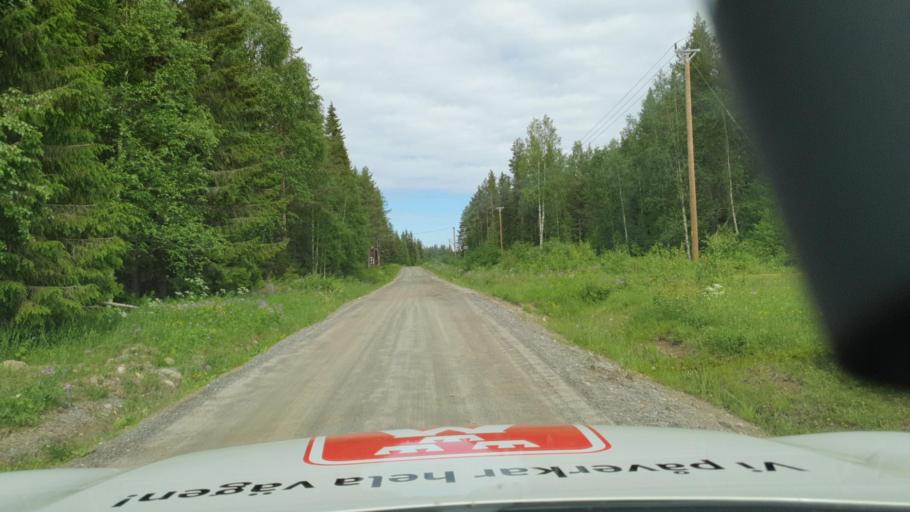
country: SE
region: Vaesterbotten
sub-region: Skelleftea Kommun
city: Langsele
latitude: 64.5748
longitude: 20.2975
